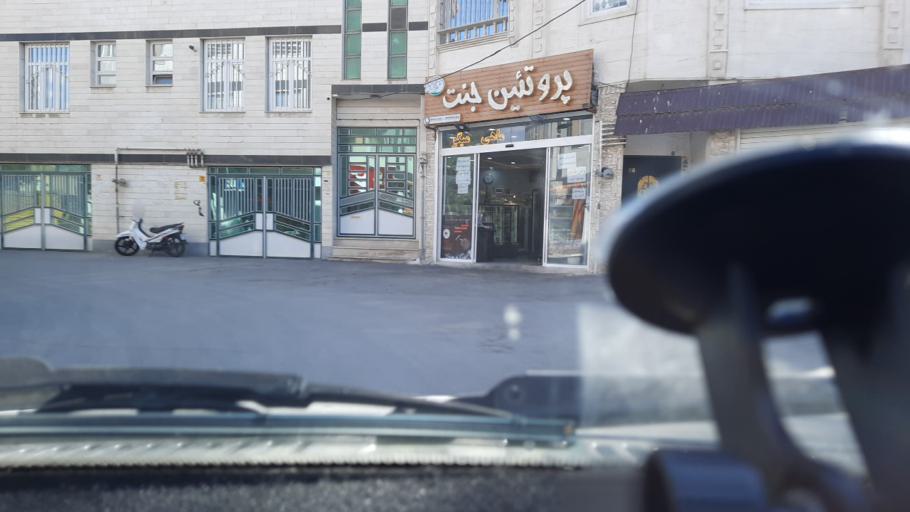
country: IR
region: Markazi
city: Arak
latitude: 34.0804
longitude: 49.6881
